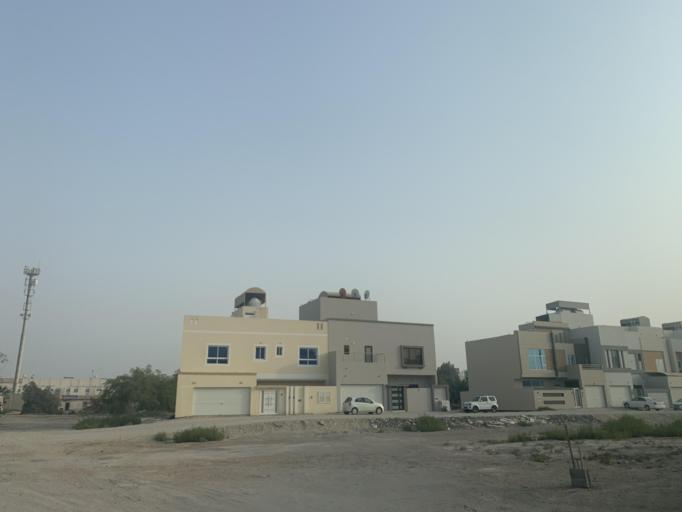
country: BH
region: Manama
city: Jidd Hafs
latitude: 26.2194
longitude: 50.5195
